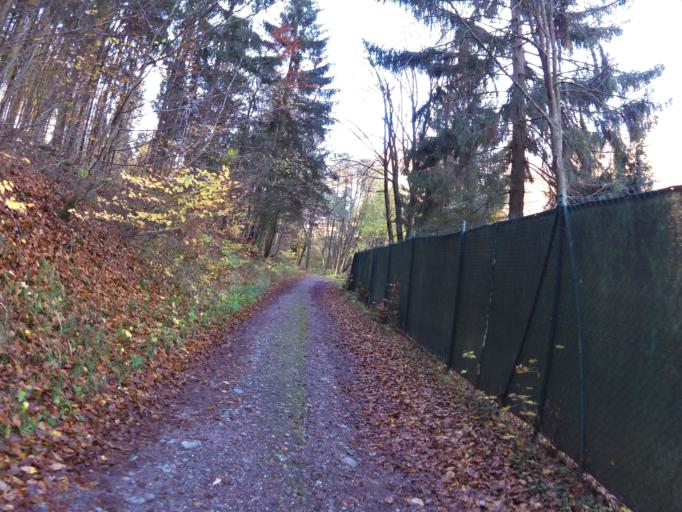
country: DE
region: Thuringia
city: Ruhla
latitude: 50.9007
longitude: 10.3519
